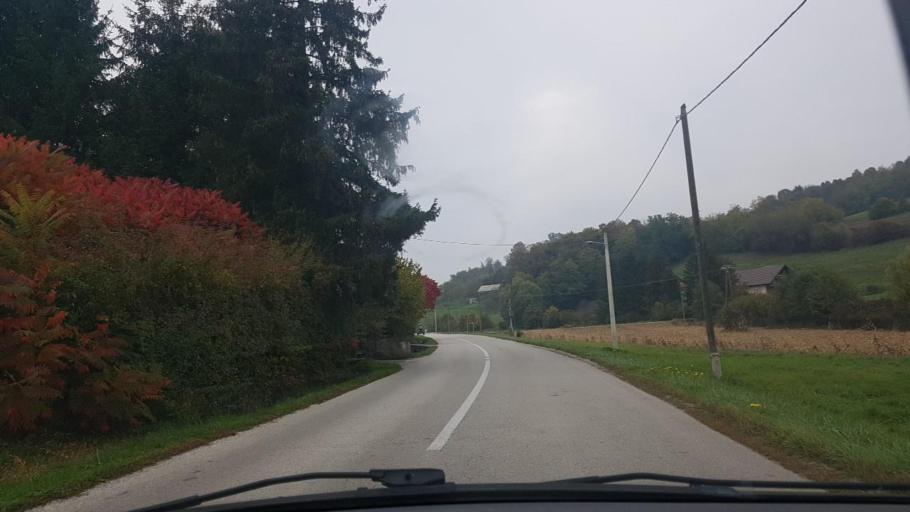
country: SI
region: Rogatec
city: Rogatec
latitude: 46.1987
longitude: 15.6972
